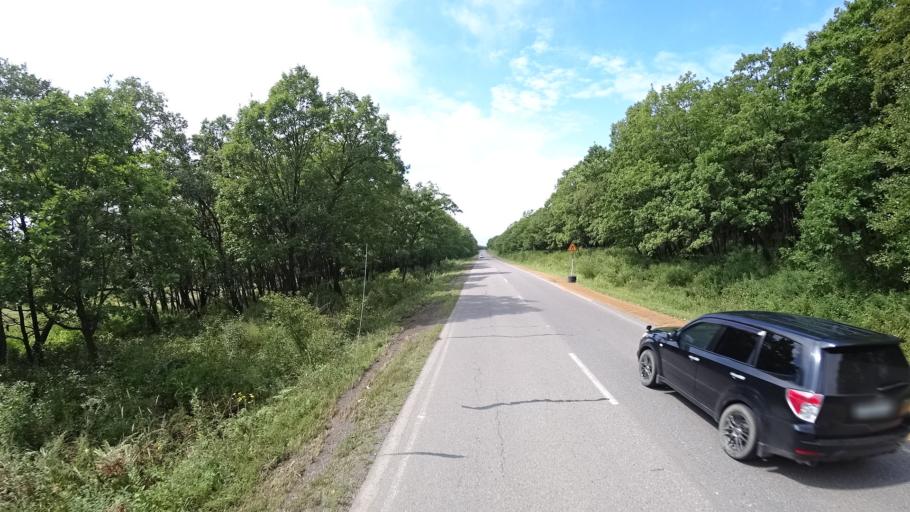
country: RU
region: Primorskiy
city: Lyalichi
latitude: 44.1406
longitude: 132.4100
